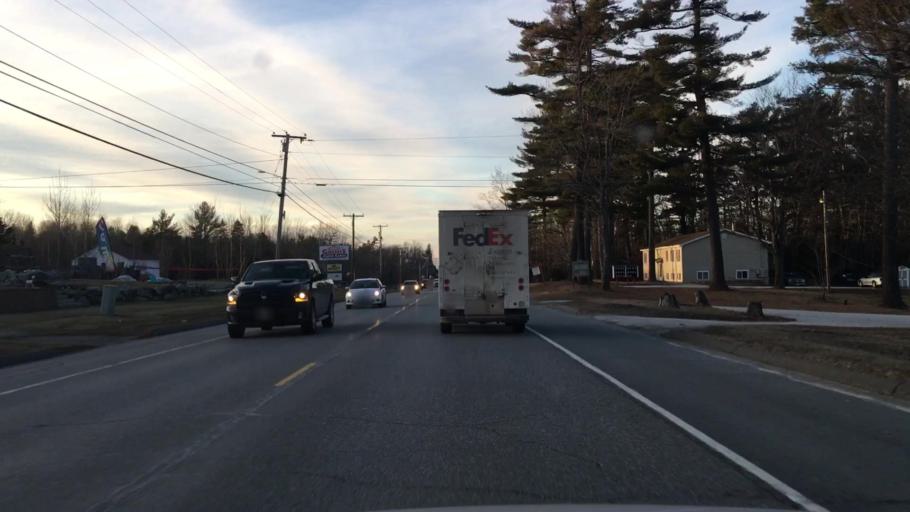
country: US
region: Maine
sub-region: Penobscot County
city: Holden
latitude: 44.7603
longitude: -68.6954
